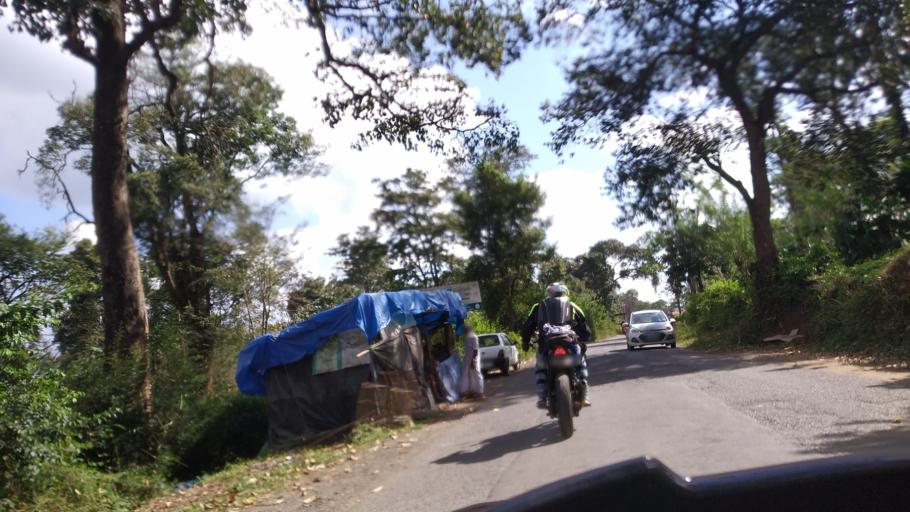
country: IN
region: Karnataka
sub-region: Kodagu
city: Ponnampet
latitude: 11.9594
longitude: 76.0623
